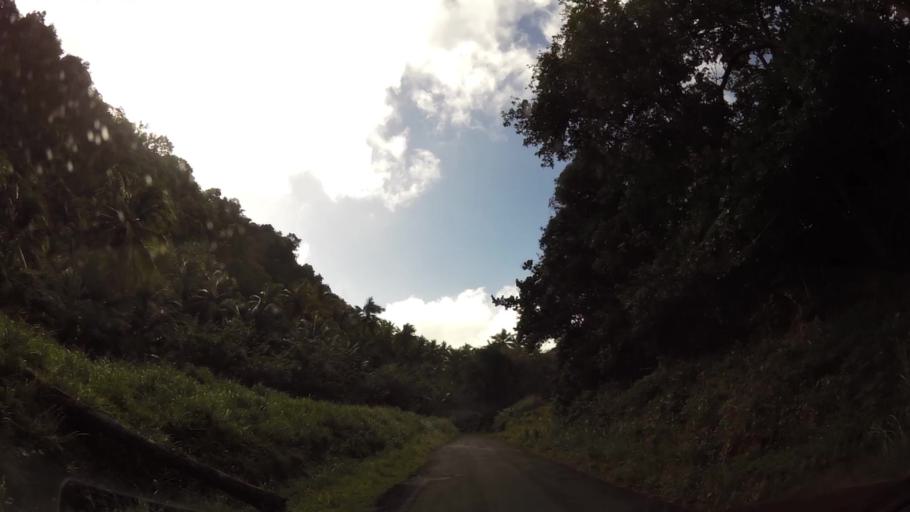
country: DM
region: Saint Andrew
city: Marigot
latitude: 15.5163
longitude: -61.2741
